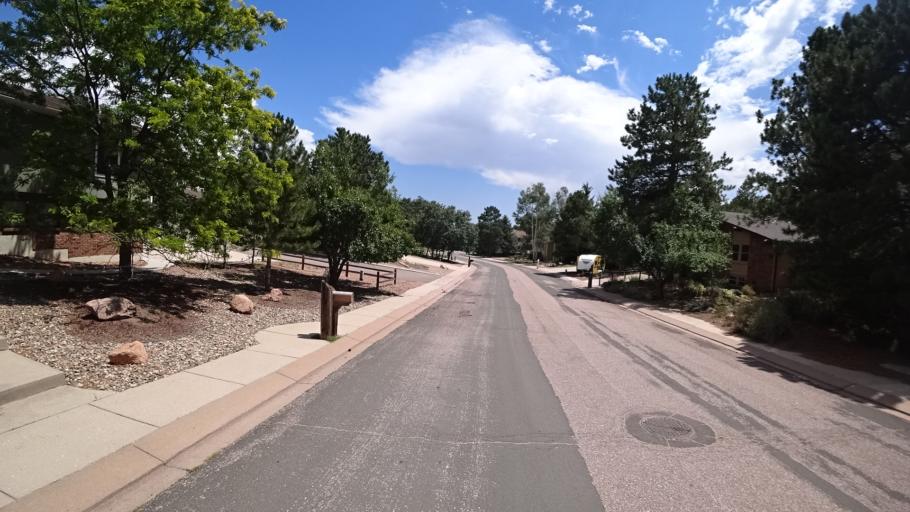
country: US
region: Colorado
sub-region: El Paso County
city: Air Force Academy
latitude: 38.9390
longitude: -104.8508
